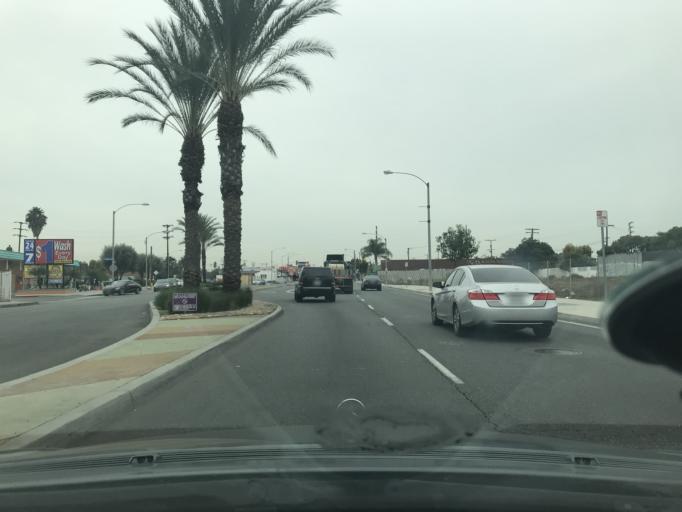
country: US
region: California
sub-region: Los Angeles County
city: Cudahy
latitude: 33.9407
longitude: -118.1817
